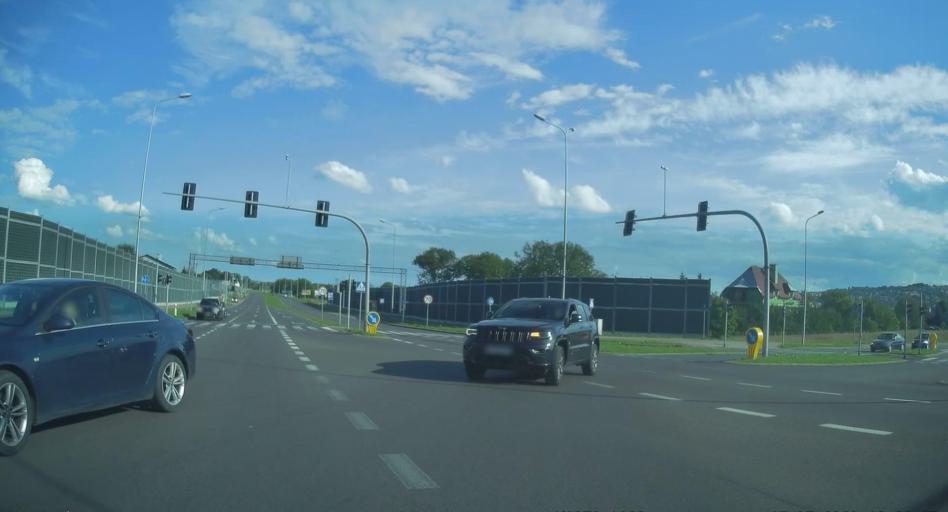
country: PL
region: Subcarpathian Voivodeship
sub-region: Przemysl
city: Przemysl
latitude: 49.7953
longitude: 22.7877
